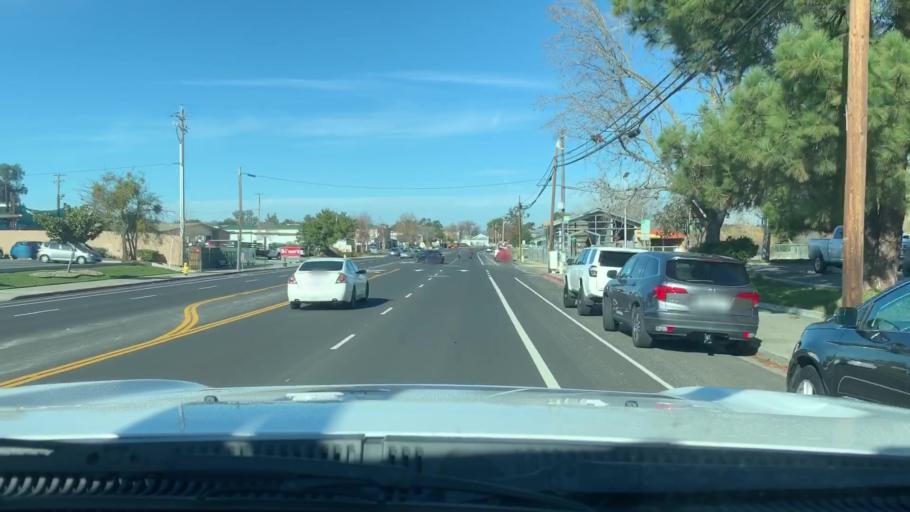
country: US
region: California
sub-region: San Luis Obispo County
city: Atascadero
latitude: 35.4672
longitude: -120.6498
